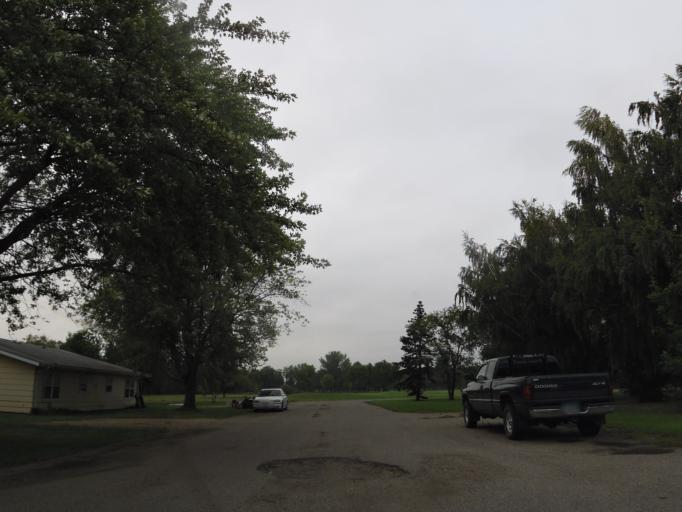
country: US
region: North Dakota
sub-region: Walsh County
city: Grafton
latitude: 48.5635
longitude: -97.1850
